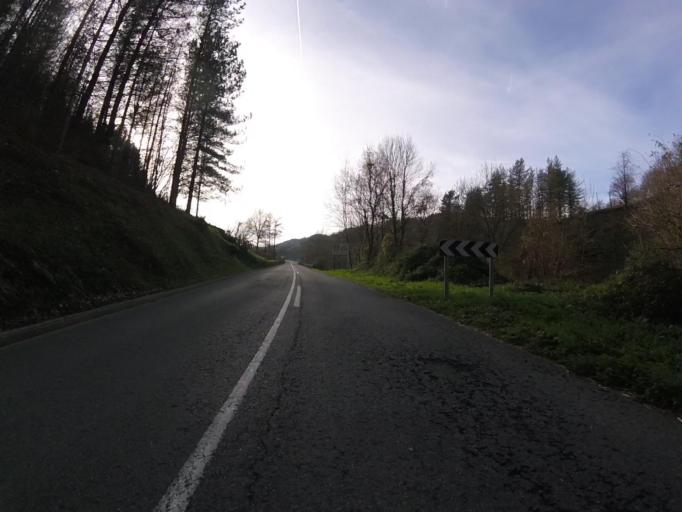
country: ES
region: Basque Country
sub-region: Provincia de Guipuzcoa
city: Berastegui
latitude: 43.1347
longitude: -1.9871
